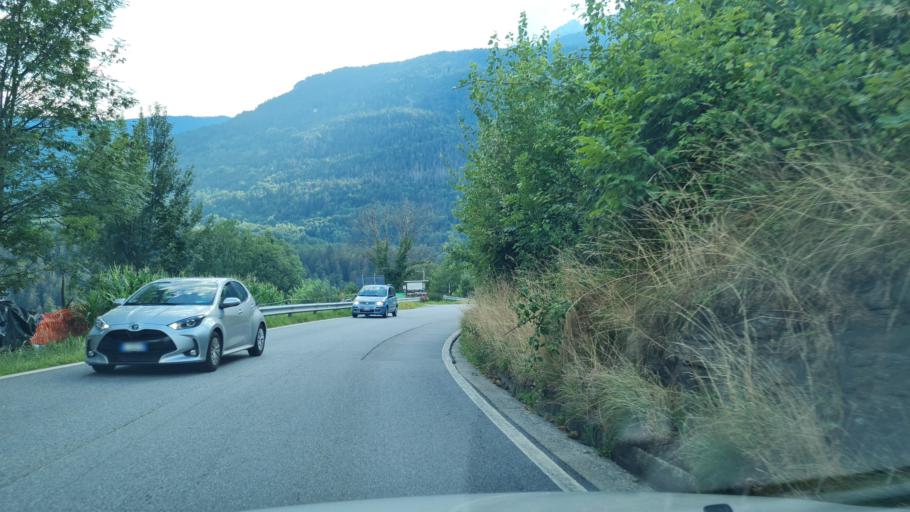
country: IT
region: Piedmont
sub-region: Provincia Verbano-Cusio-Ossola
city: Baceno
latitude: 46.2562
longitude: 8.3251
